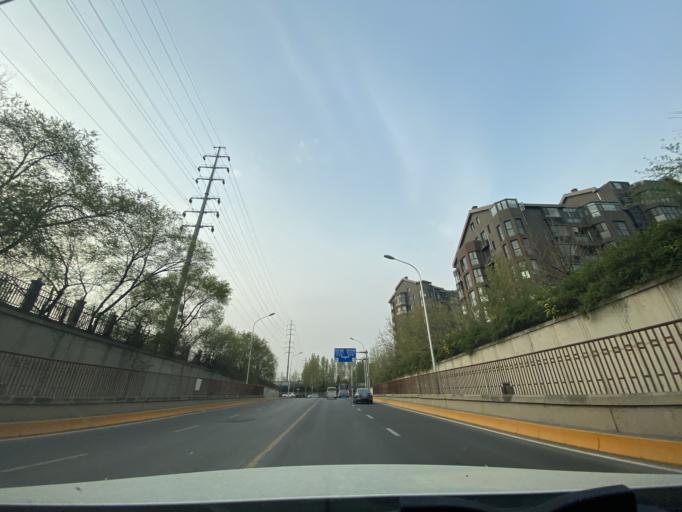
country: CN
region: Beijing
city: Babaoshan
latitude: 39.9315
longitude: 116.2326
